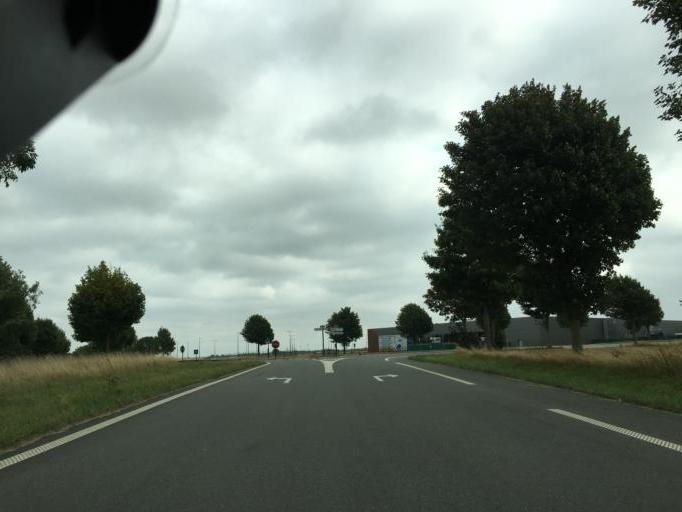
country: FR
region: Nord-Pas-de-Calais
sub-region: Departement du Pas-de-Calais
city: Saint-Pol-sur-Ternoise
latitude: 50.3670
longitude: 2.3296
